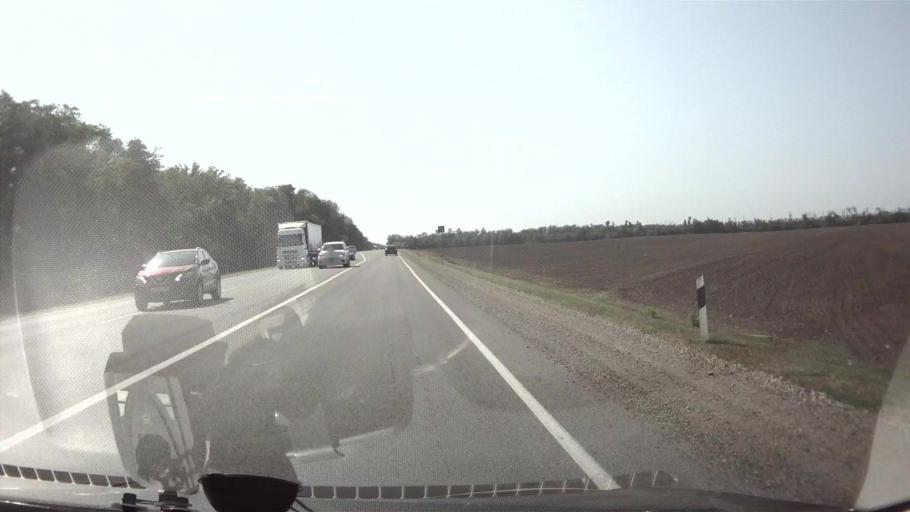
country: RU
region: Krasnodarskiy
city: Vasyurinskaya
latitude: 45.1484
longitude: 39.4364
